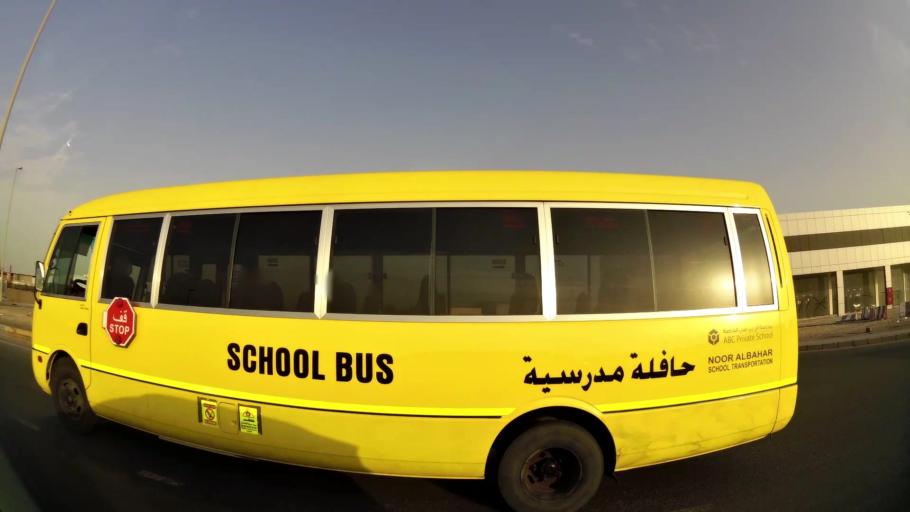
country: AE
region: Abu Dhabi
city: Abu Dhabi
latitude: 24.3682
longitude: 54.5016
